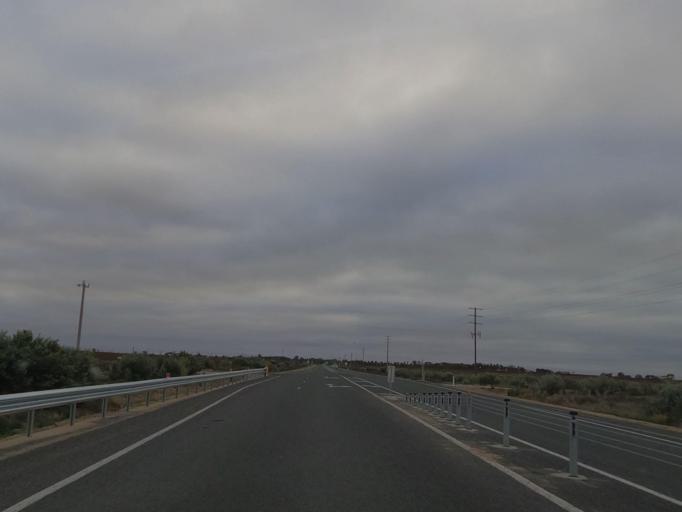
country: AU
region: Victoria
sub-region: Swan Hill
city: Swan Hill
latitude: -35.4743
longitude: 143.6755
